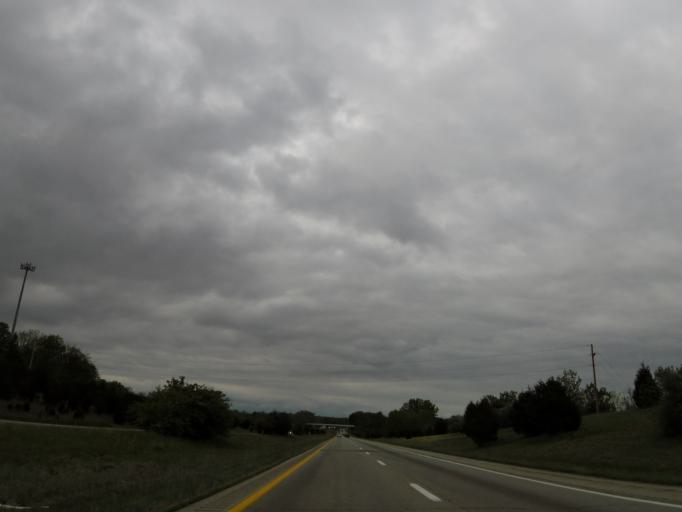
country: US
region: Ohio
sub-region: Franklin County
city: Grove City
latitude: 39.8171
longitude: -83.1788
